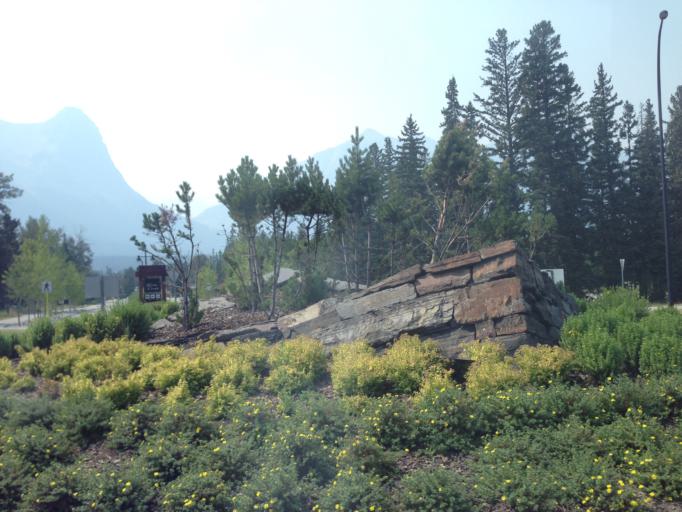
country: CA
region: Alberta
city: Canmore
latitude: 51.0848
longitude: -115.3443
